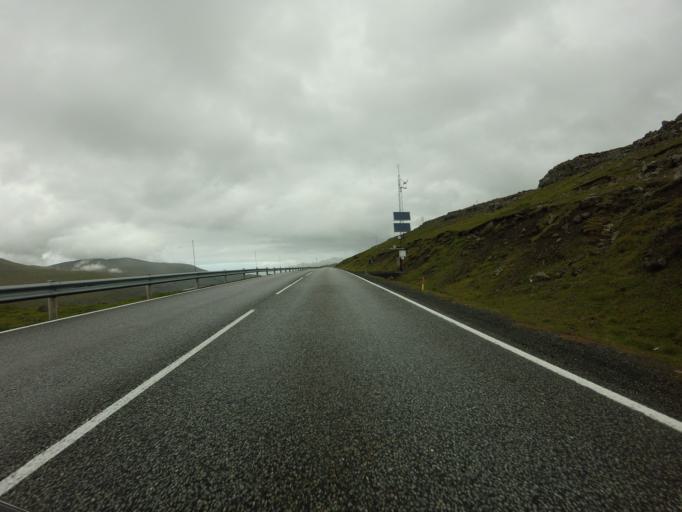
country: FO
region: Streymoy
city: Vestmanna
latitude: 62.1264
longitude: -7.1499
